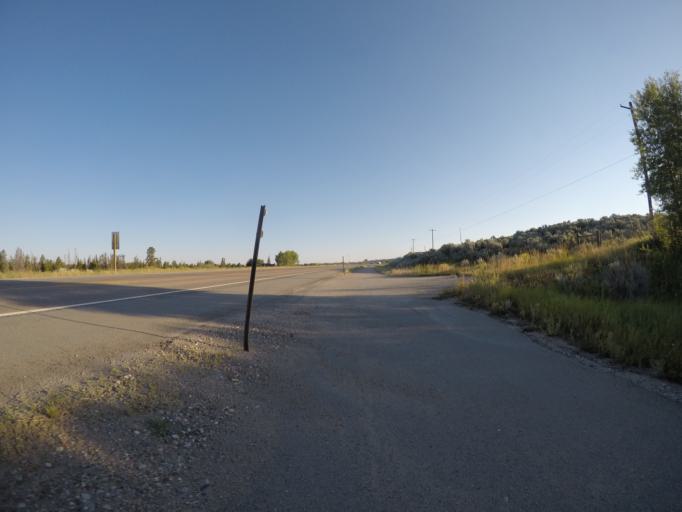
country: US
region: Wyoming
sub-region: Sublette County
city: Pinedale
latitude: 42.8508
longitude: -109.8498
